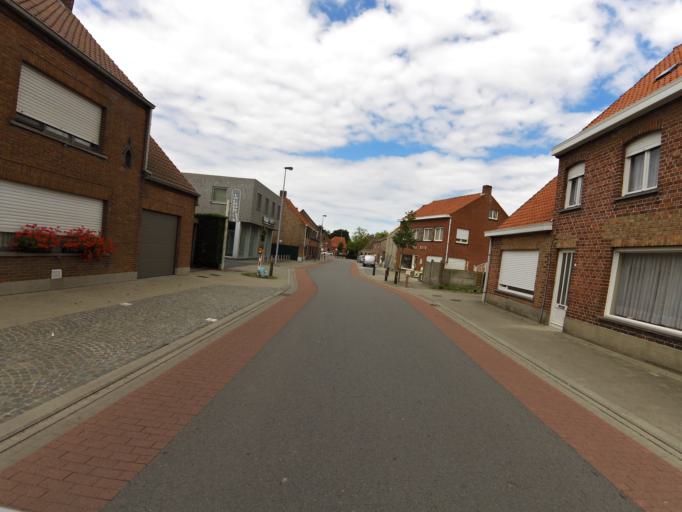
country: BE
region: Flanders
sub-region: Provincie West-Vlaanderen
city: Koekelare
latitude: 51.0958
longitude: 2.9802
